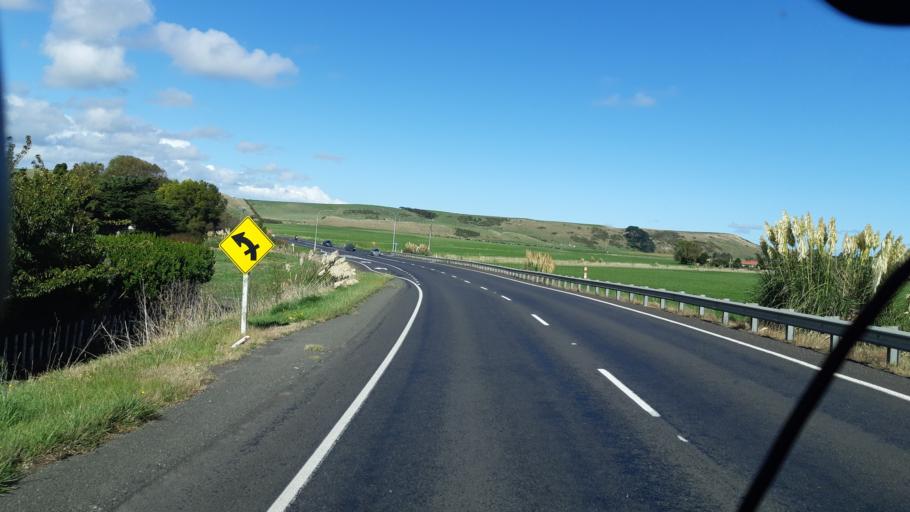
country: NZ
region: Manawatu-Wanganui
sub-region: Wanganui District
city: Wanganui
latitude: -40.0064
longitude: 175.1671
